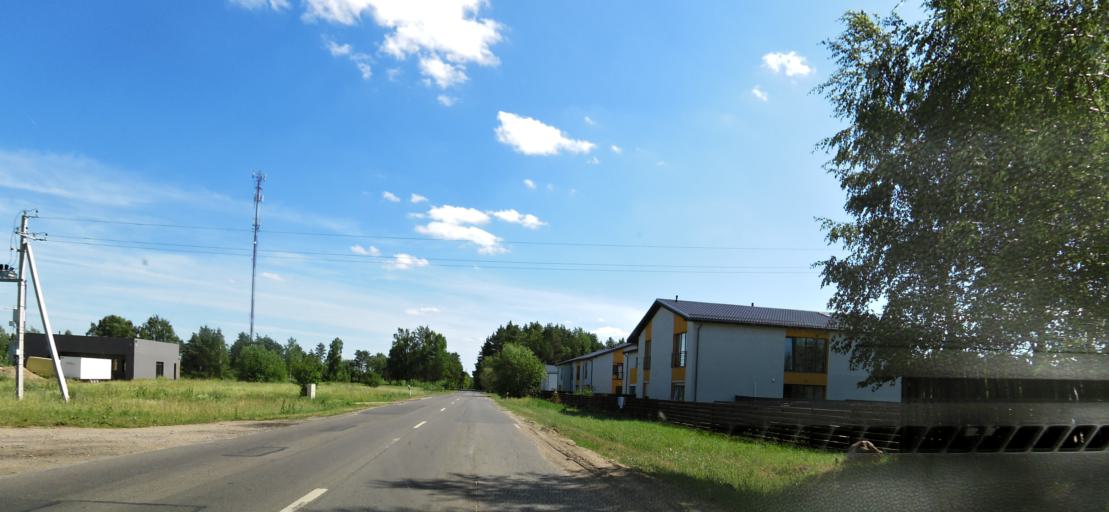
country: LT
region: Vilnius County
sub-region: Vilnius
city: Fabijoniskes
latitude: 54.7992
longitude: 25.3487
